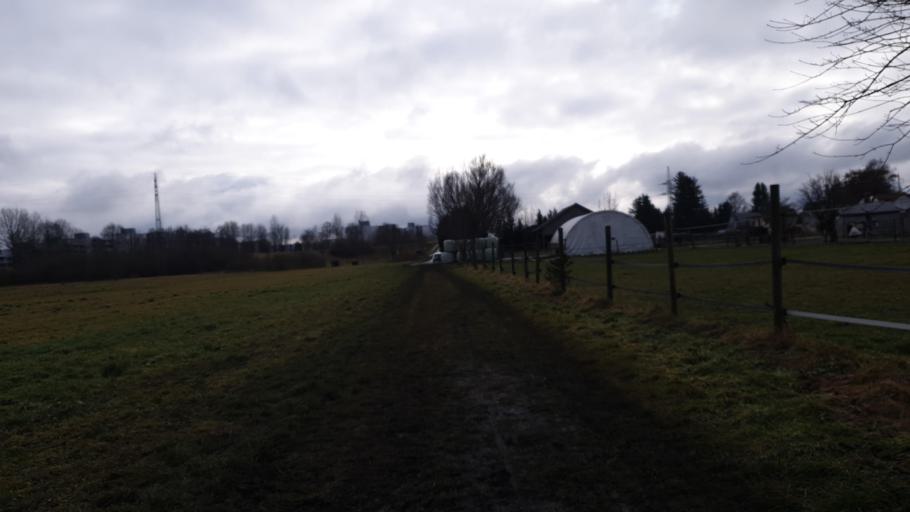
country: DE
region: Bavaria
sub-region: Upper Bavaria
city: Germering
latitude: 48.1662
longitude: 11.4079
